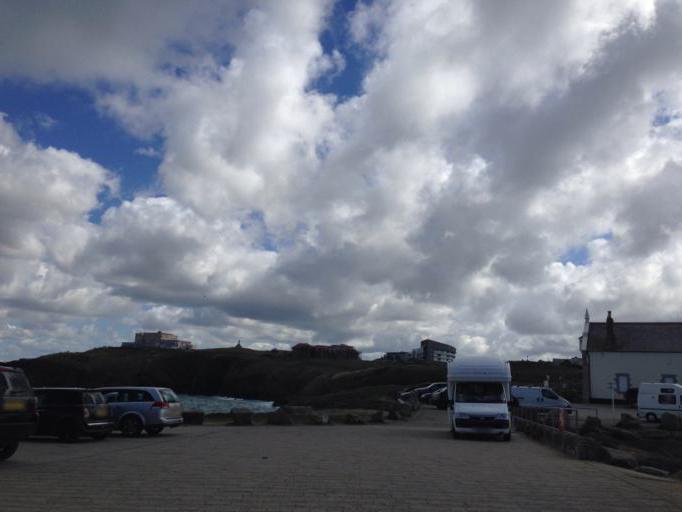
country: GB
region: England
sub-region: Cornwall
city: Newquay
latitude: 50.4236
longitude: -5.0976
